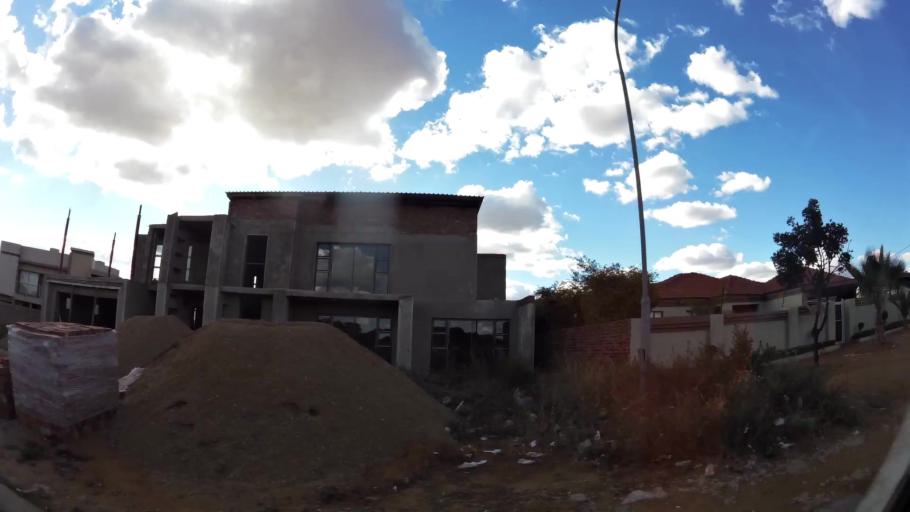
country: ZA
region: Limpopo
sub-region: Capricorn District Municipality
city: Polokwane
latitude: -23.9127
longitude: 29.4955
